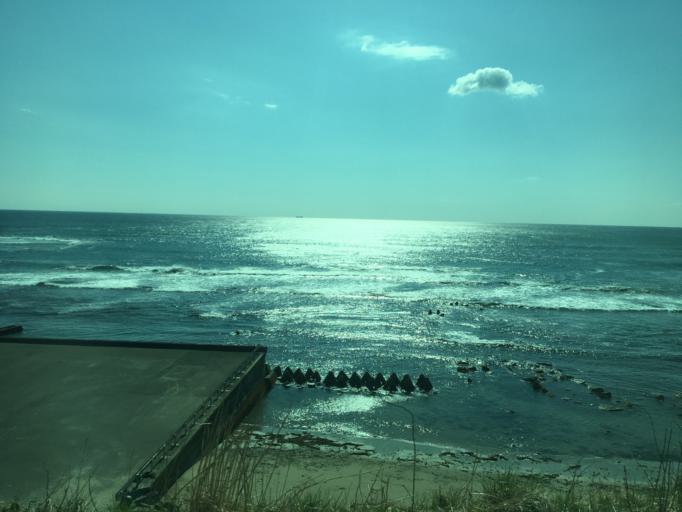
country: JP
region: Aomori
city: Hachinohe
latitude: 40.3412
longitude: 141.7708
